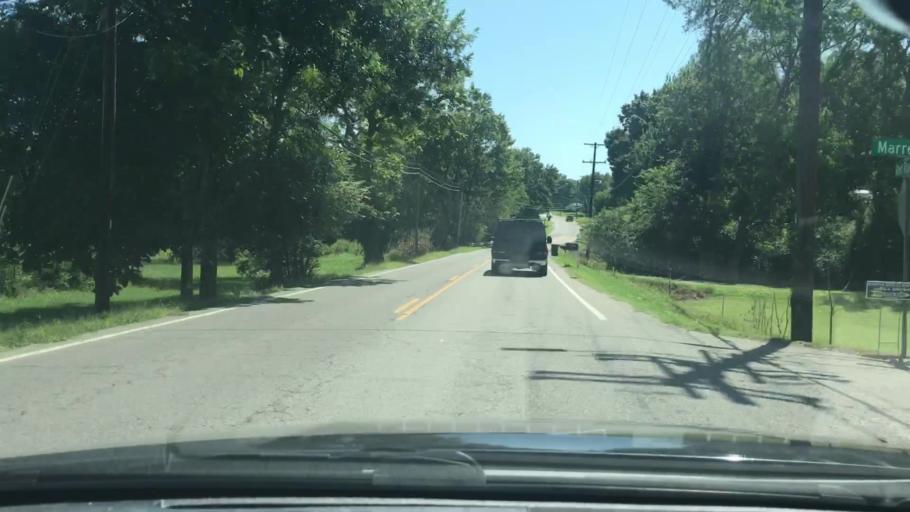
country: US
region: Tennessee
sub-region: Sumner County
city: Gallatin
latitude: 36.3953
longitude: -86.4706
